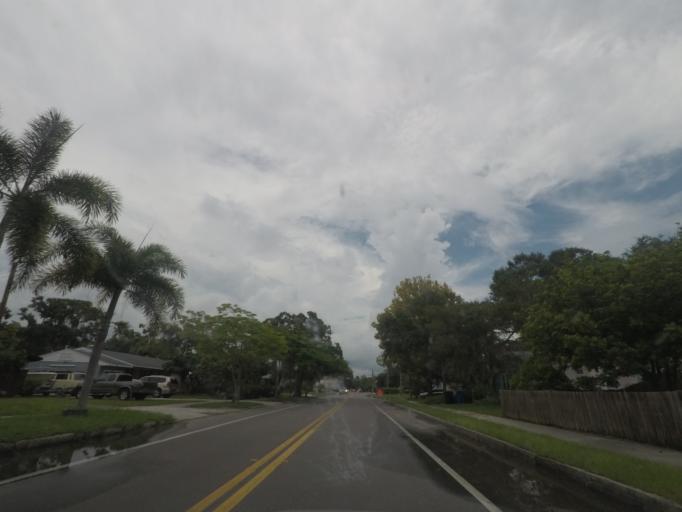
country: US
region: Florida
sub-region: Pinellas County
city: Lealman
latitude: 27.7993
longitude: -82.6485
